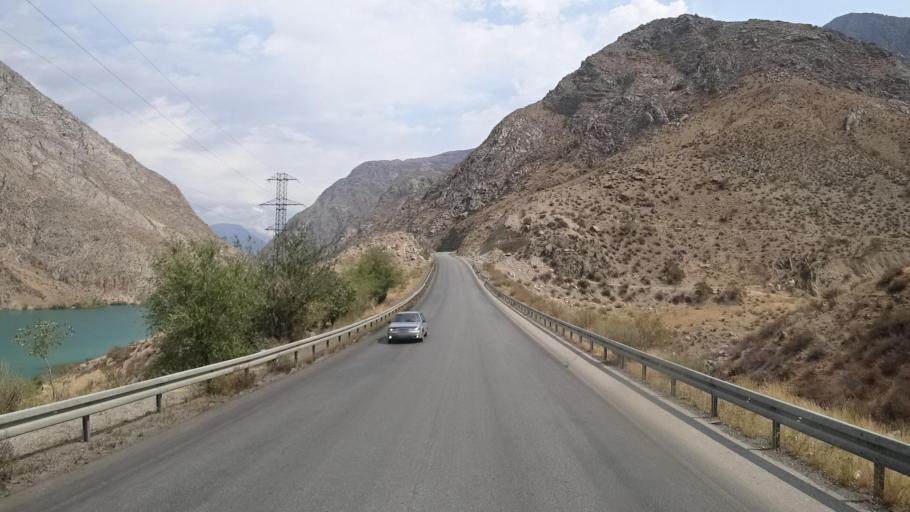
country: KG
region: Jalal-Abad
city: Tash-Kumyr
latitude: 41.5469
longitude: 72.4942
